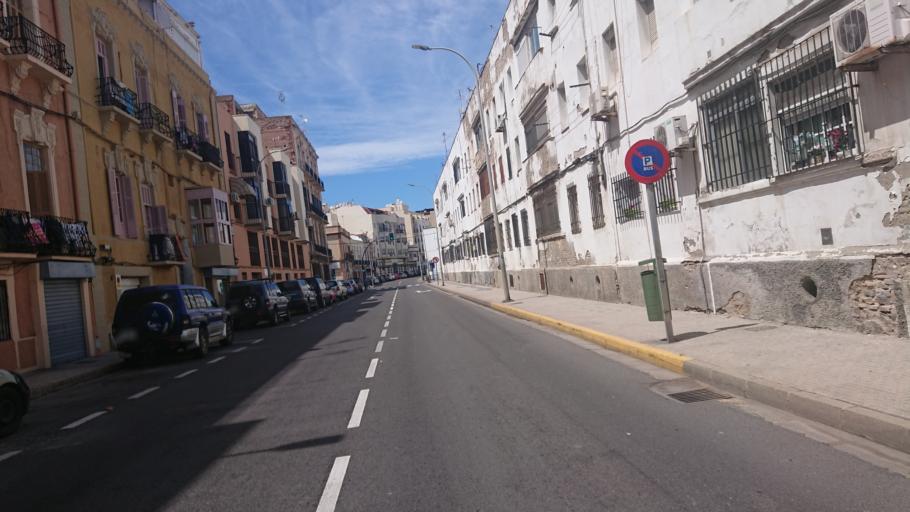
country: ES
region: Melilla
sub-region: Melilla
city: Melilla
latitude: 35.2838
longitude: -2.9413
